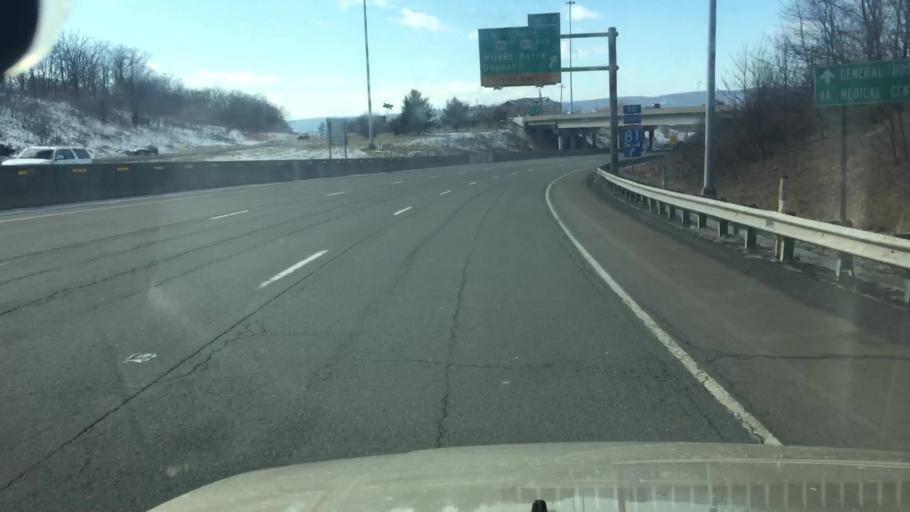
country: US
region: Pennsylvania
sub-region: Luzerne County
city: Hudson
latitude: 41.2510
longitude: -75.8322
